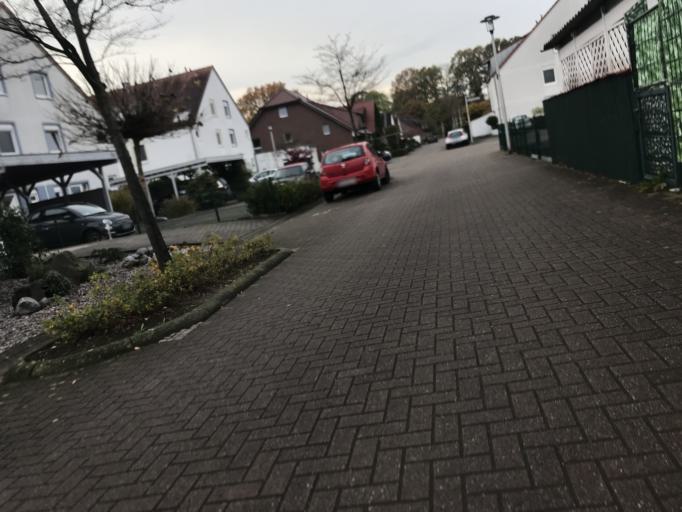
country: DE
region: North Rhine-Westphalia
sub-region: Regierungsbezirk Arnsberg
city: Hamm
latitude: 51.6883
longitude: 7.8669
